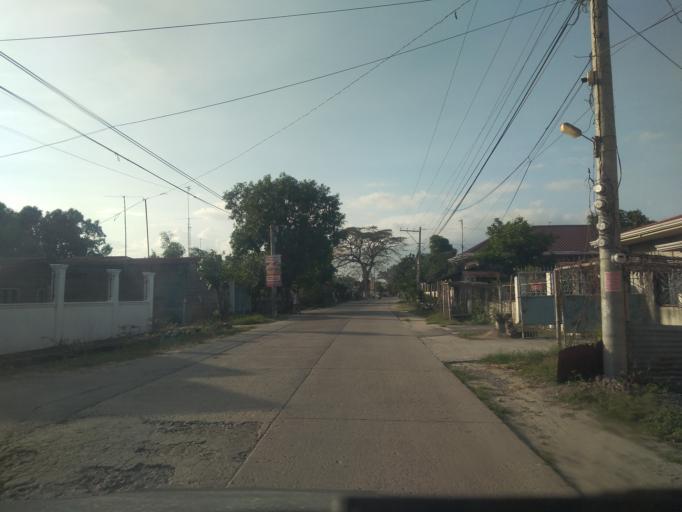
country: PH
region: Central Luzon
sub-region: Province of Pampanga
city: Bulaon
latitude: 15.0906
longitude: 120.6874
